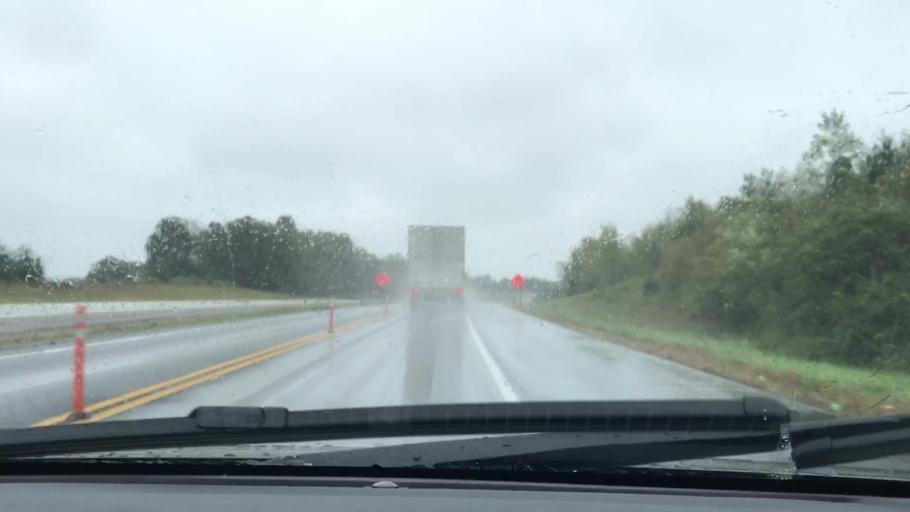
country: US
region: Kentucky
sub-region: Christian County
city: Hopkinsville
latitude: 37.0144
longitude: -87.4573
